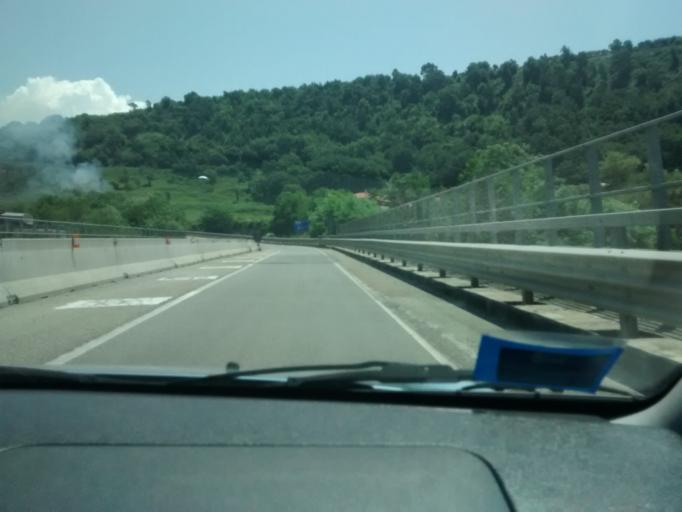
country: IT
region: Calabria
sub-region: Provincia di Catanzaro
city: Maida
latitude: 38.9024
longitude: 16.3862
